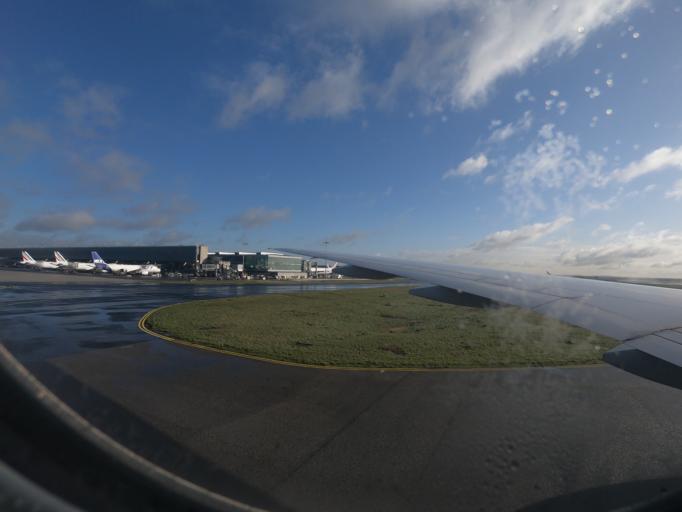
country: FR
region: Ile-de-France
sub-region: Departement de Seine-et-Marne
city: Mitry-Mory
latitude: 48.9995
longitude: 2.5825
